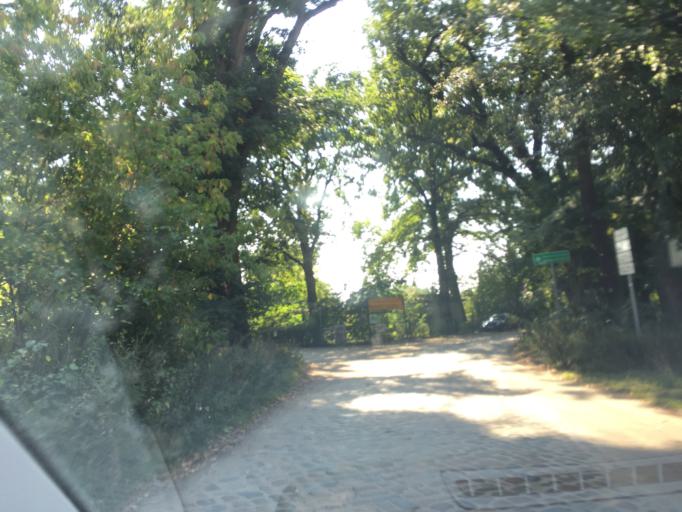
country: DE
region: Berlin
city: Rahnsdorf
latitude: 52.4348
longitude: 13.6951
